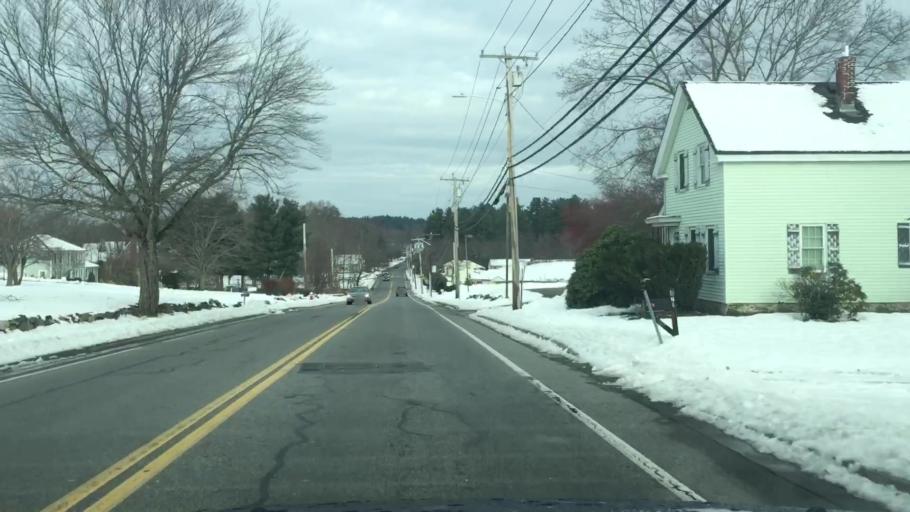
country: US
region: Massachusetts
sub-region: Middlesex County
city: Dracut
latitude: 42.6718
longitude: -71.3511
